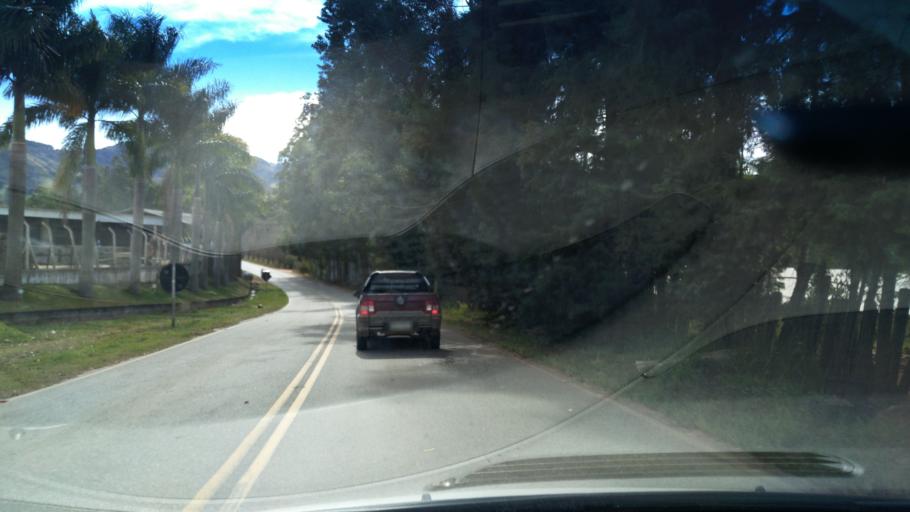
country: BR
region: Minas Gerais
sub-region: Andradas
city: Andradas
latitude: -22.0650
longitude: -46.4366
